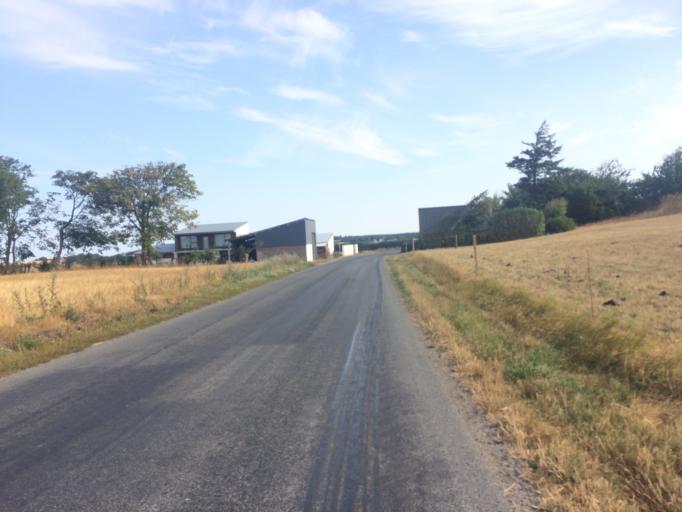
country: DK
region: Central Jutland
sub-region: Holstebro Kommune
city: Vinderup
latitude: 56.5921
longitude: 8.7565
